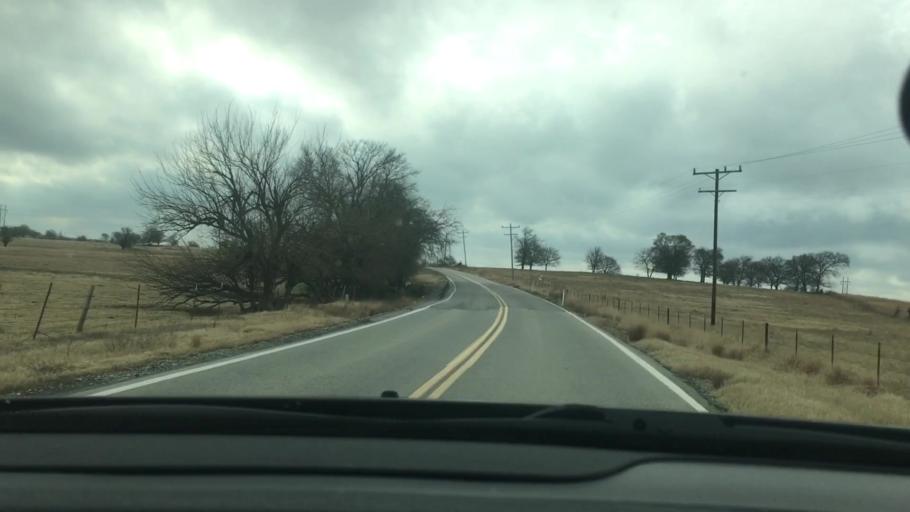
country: US
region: Oklahoma
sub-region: Bryan County
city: Durant
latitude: 34.0958
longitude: -96.4875
